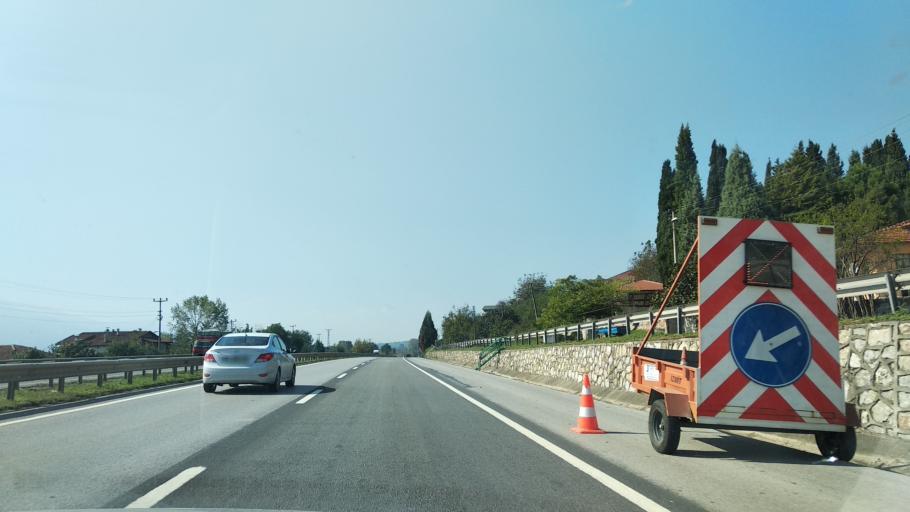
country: TR
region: Sakarya
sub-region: Merkez
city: Sapanca
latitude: 40.7334
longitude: 30.2163
